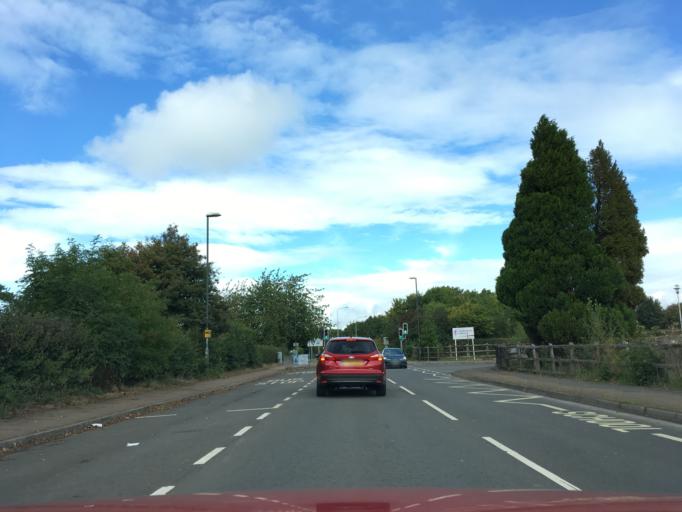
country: GB
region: Wales
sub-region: Monmouthshire
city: Chepstow
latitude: 51.6418
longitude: -2.6614
